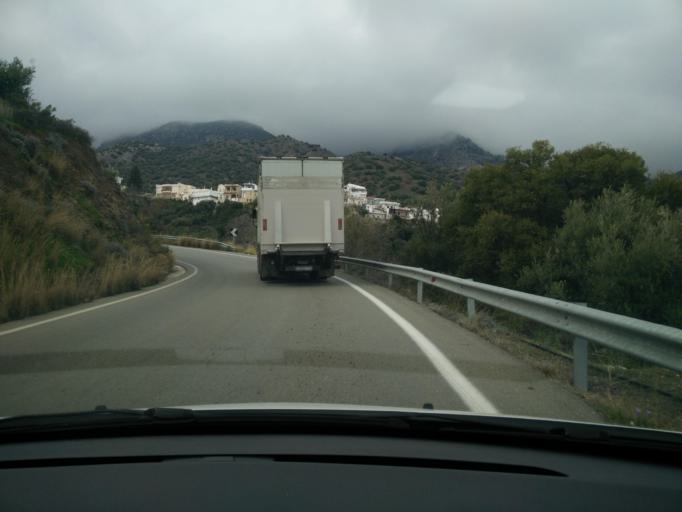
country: GR
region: Crete
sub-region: Nomos Lasithiou
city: Gra Liyia
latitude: 35.0263
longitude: 25.5690
